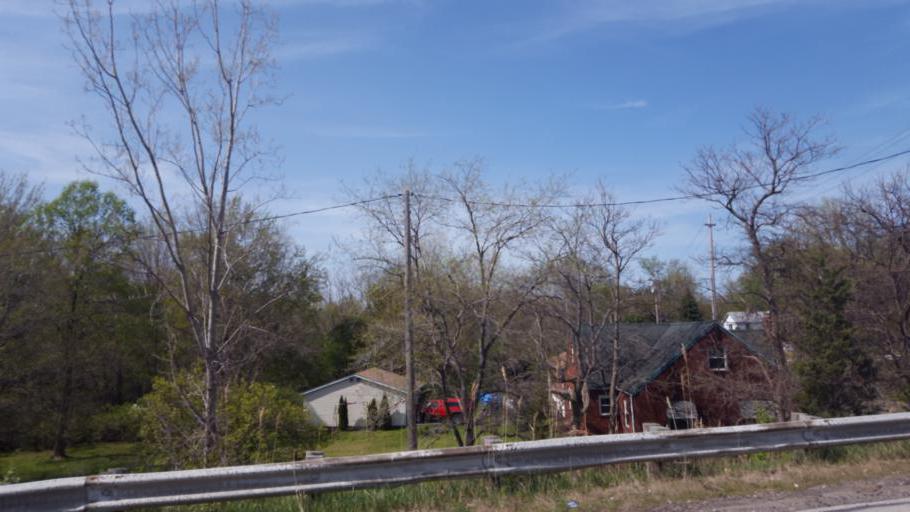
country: US
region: Ohio
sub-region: Lake County
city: Fairport Harbor
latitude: 41.7264
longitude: -81.2699
